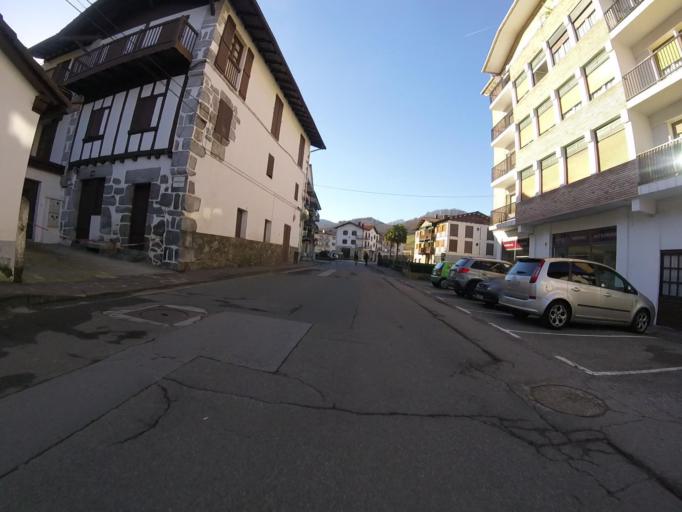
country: ES
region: Navarre
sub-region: Provincia de Navarra
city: Lesaka
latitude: 43.2469
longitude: -1.7071
